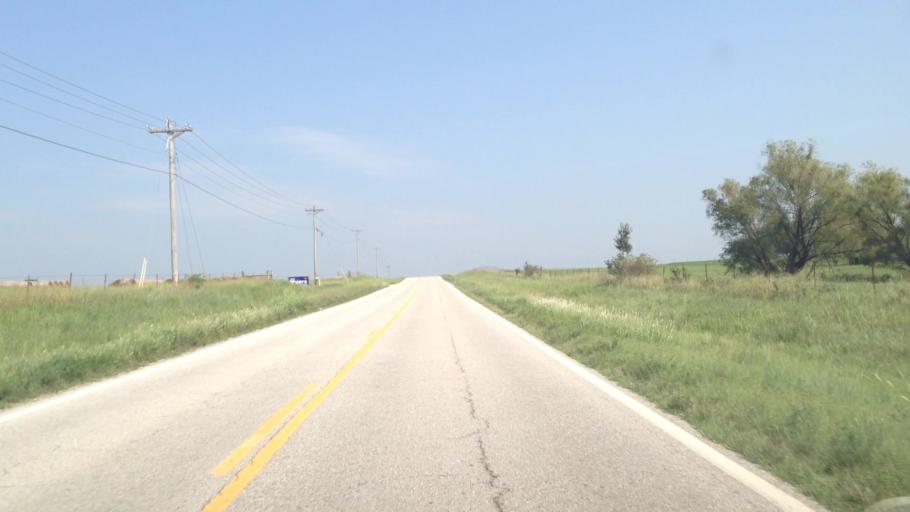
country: US
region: Oklahoma
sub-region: Craig County
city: Vinita
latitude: 36.7378
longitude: -95.1436
